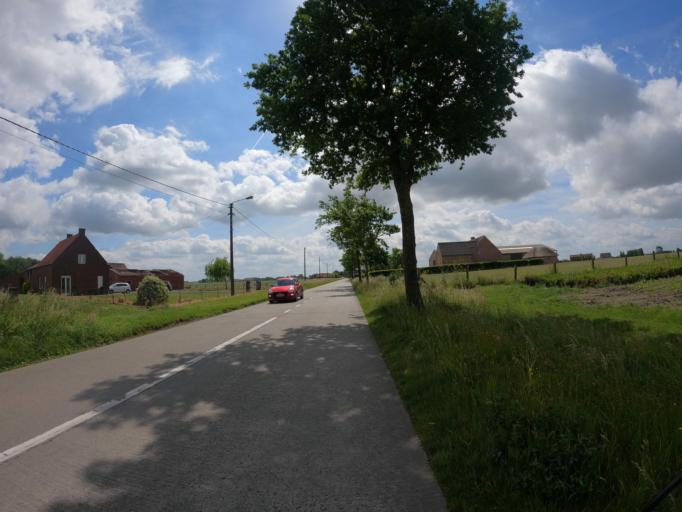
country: BE
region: Flanders
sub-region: Provincie West-Vlaanderen
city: Ruiselede
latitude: 51.0671
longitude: 3.3686
